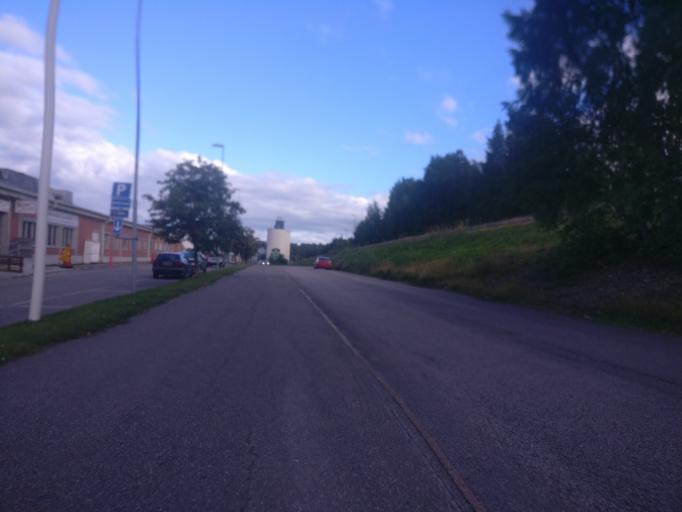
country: SE
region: Vaesternorrland
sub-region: Sundsvalls Kommun
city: Sundsvall
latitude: 62.3853
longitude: 17.3302
